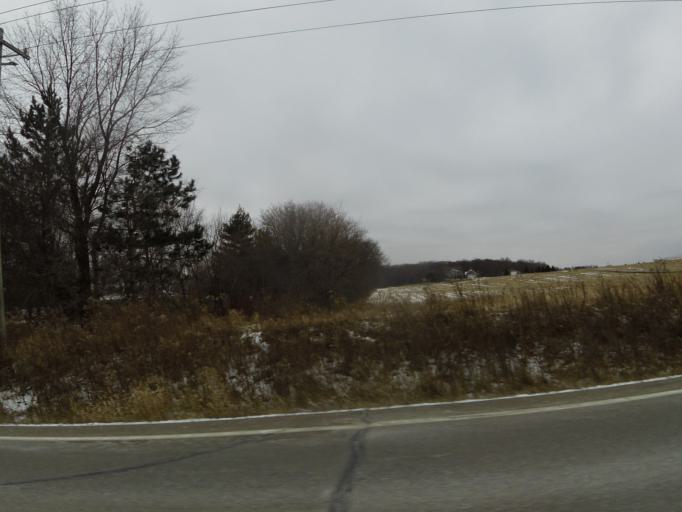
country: US
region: Minnesota
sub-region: Hennepin County
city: Independence
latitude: 45.0232
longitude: -93.7274
